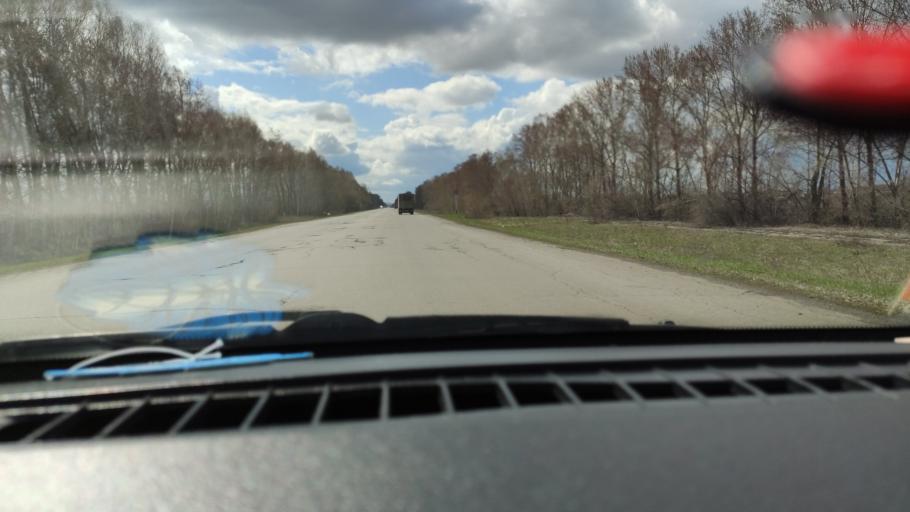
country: RU
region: Samara
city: Tol'yatti
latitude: 53.6355
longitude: 49.4187
